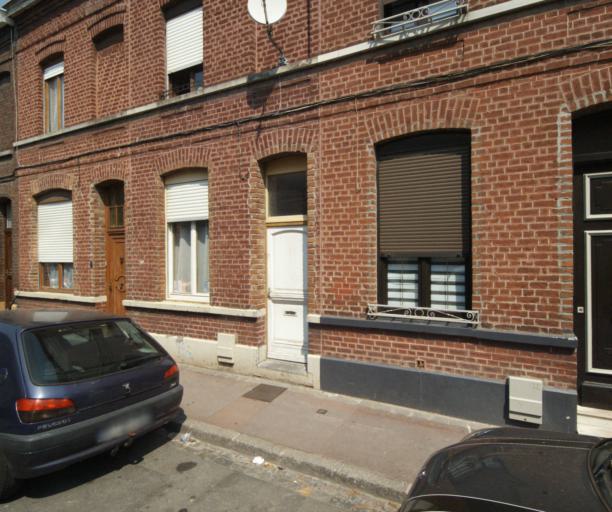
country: FR
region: Nord-Pas-de-Calais
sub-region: Departement du Nord
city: Tourcoing
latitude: 50.7229
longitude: 3.1442
